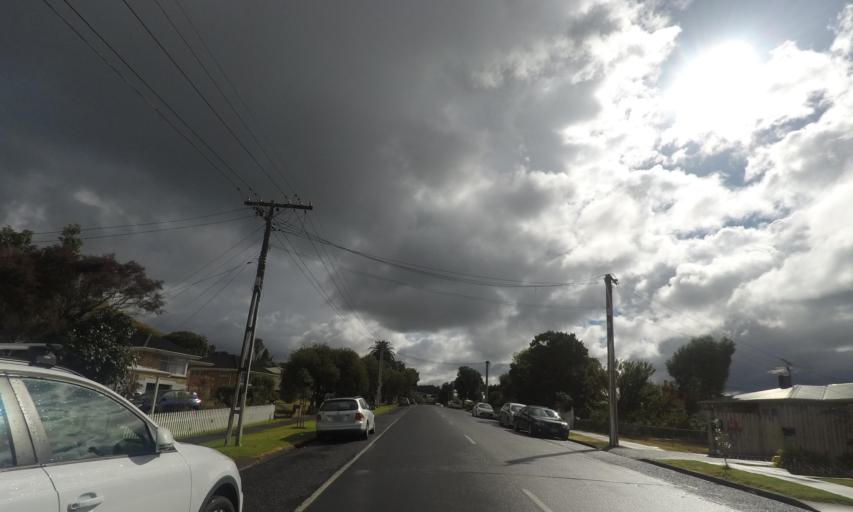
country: NZ
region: Auckland
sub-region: Auckland
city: Mangere
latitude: -36.9531
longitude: 174.7860
